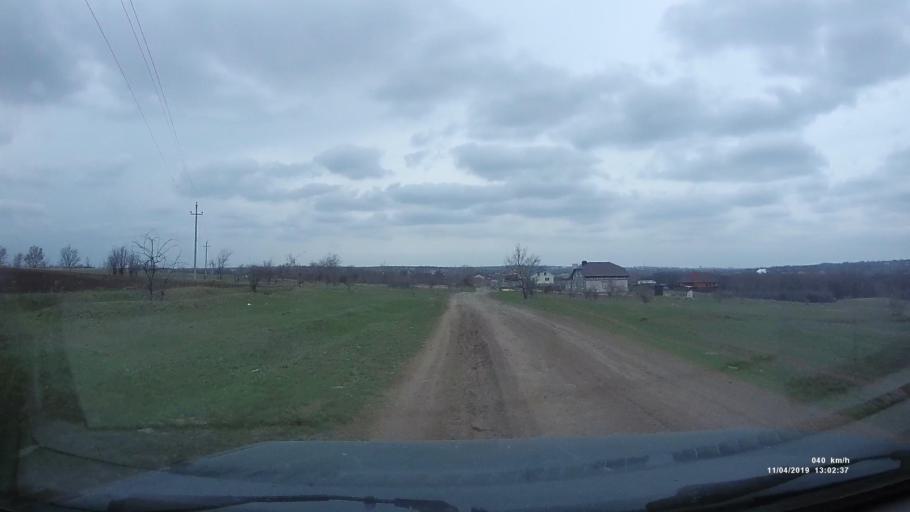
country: RU
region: Rostov
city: Staraya Stanitsa
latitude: 48.2879
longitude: 40.3566
